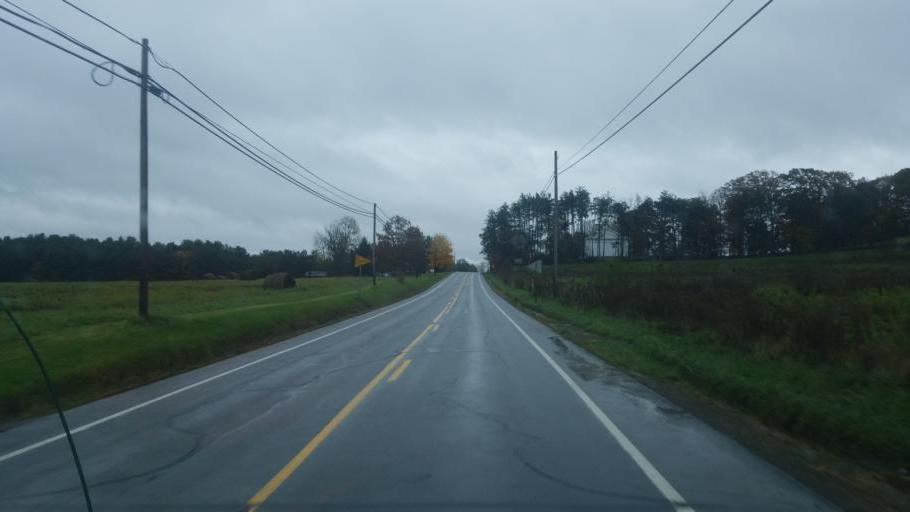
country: US
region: Pennsylvania
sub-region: Jefferson County
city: Brookville
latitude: 41.1803
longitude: -79.2138
